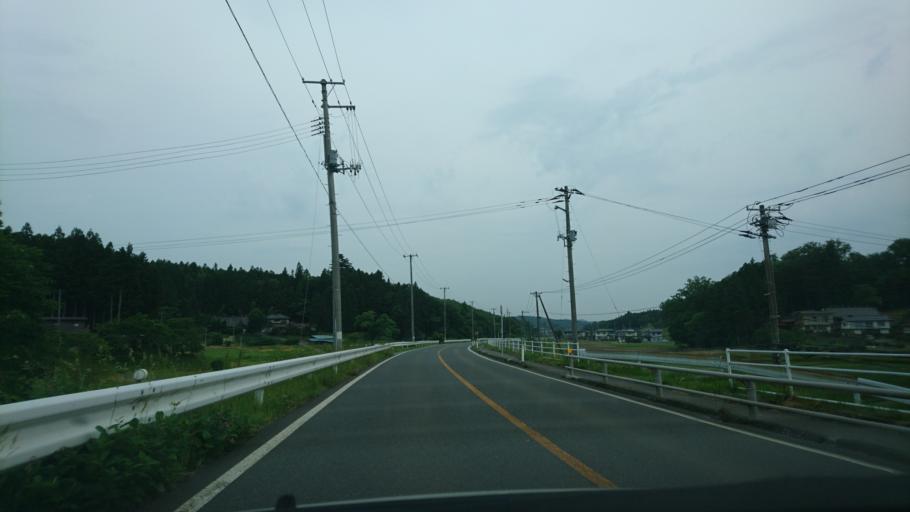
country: JP
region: Iwate
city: Ichinoseki
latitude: 38.8870
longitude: 141.1333
